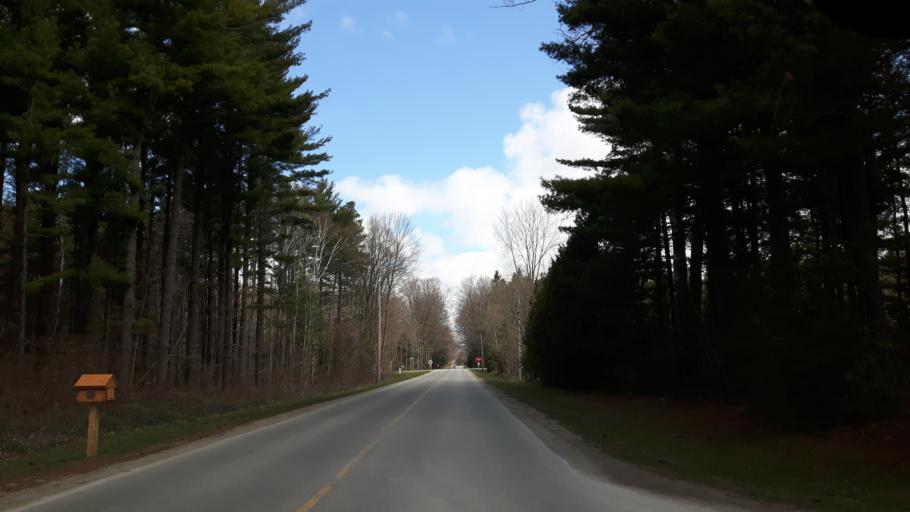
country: CA
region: Ontario
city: Goderich
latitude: 43.6042
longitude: -81.6847
